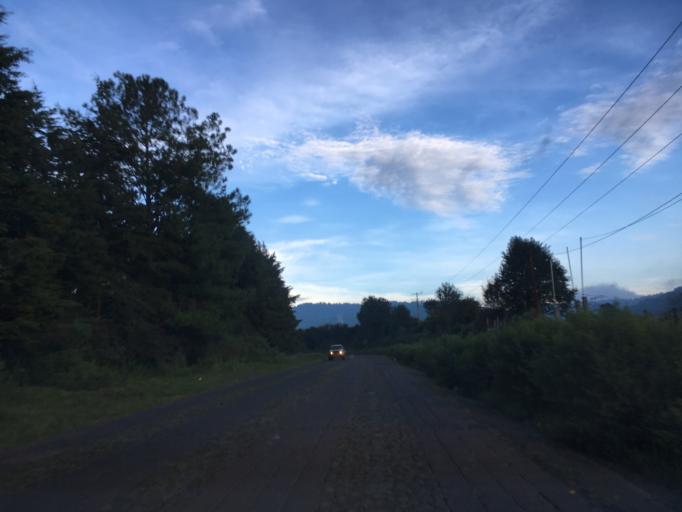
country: MX
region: Michoacan
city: Villa Escalante
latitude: 19.4080
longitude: -101.6897
